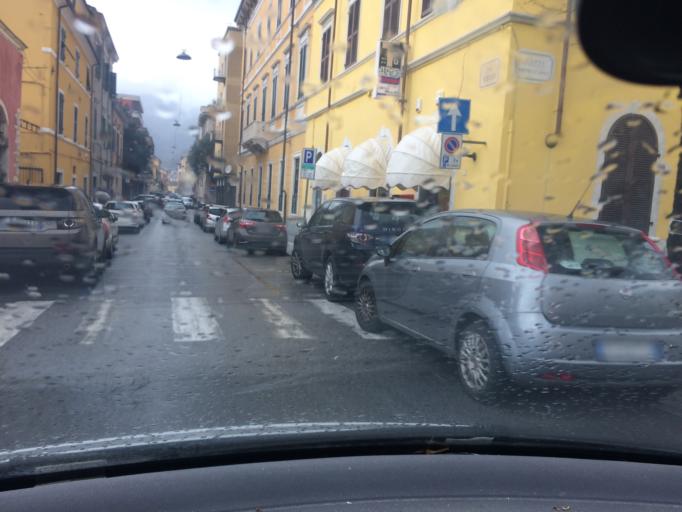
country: IT
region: Tuscany
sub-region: Provincia di Massa-Carrara
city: Carrara
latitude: 44.0759
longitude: 10.1026
